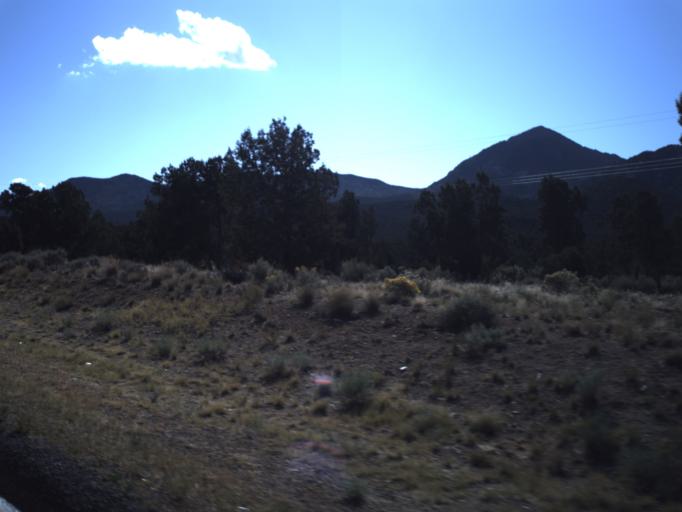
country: US
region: Utah
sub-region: Washington County
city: Enterprise
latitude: 37.6112
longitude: -113.3967
